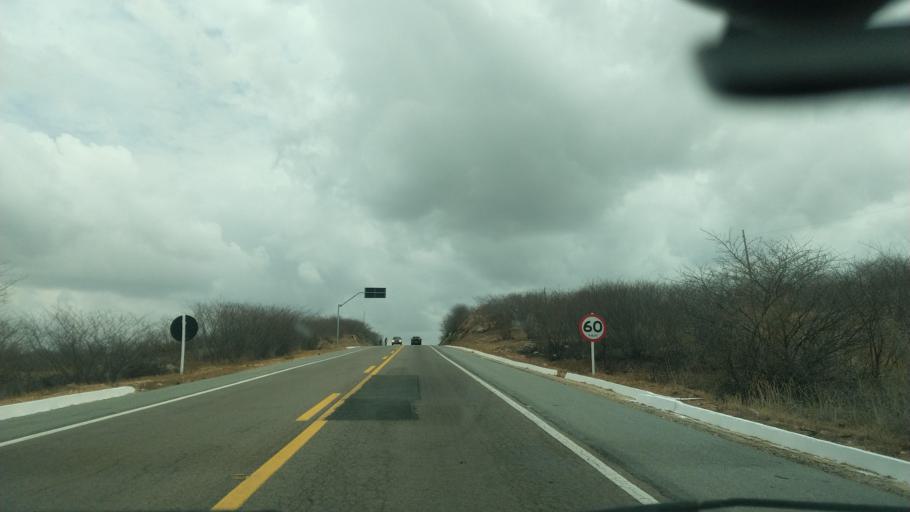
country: BR
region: Rio Grande do Norte
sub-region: Currais Novos
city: Currais Novos
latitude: -6.2171
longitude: -36.4241
